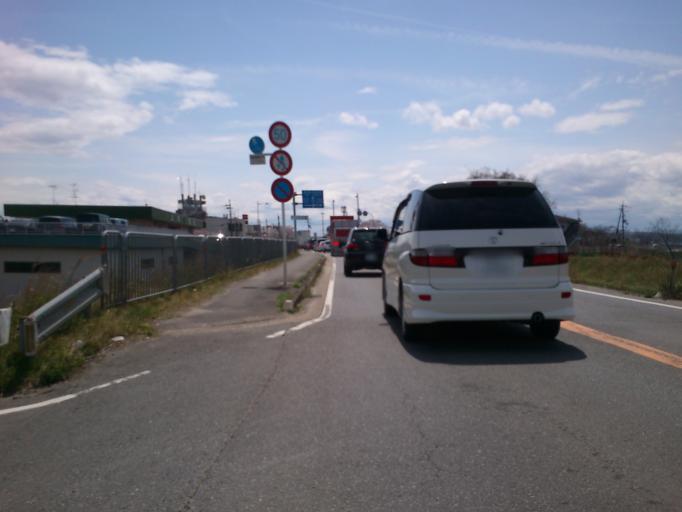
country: JP
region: Kyoto
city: Tanabe
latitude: 34.8003
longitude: 135.8030
